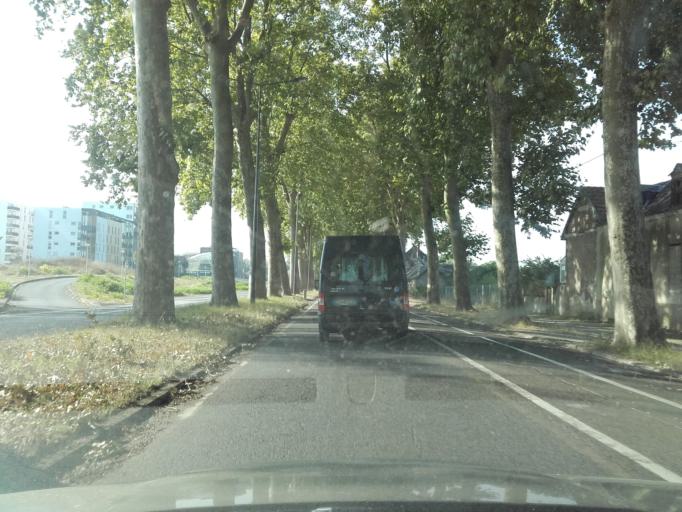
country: FR
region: Centre
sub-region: Departement d'Indre-et-Loire
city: Tours
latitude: 47.3698
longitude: 0.6769
